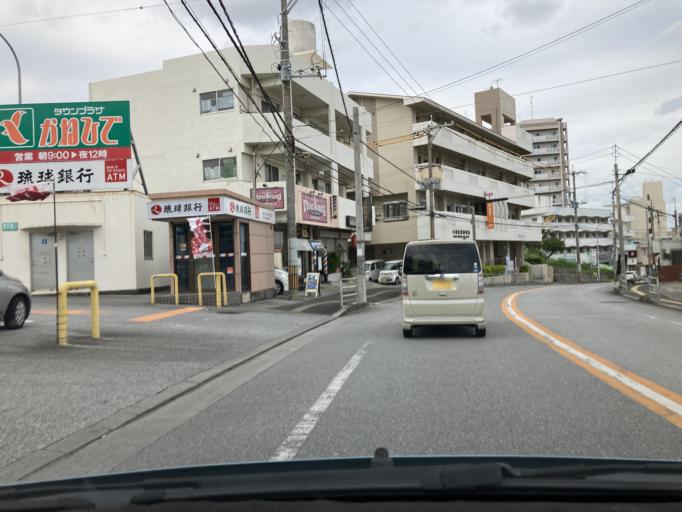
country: JP
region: Okinawa
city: Tomigusuku
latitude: 26.1905
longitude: 127.6790
